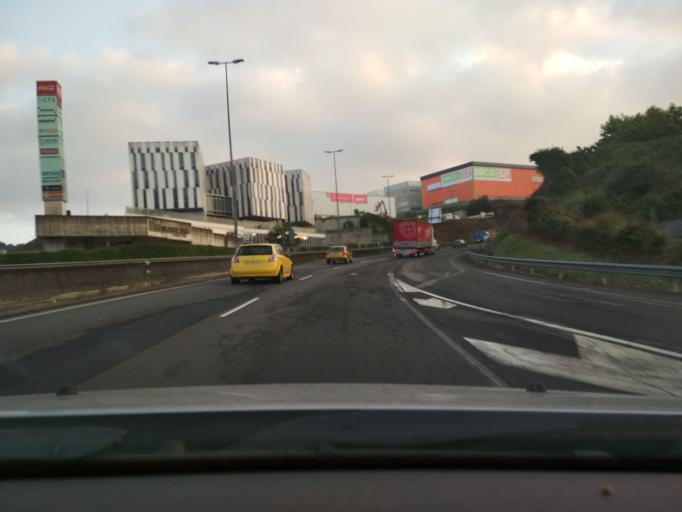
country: ES
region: Galicia
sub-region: Provincia da Coruna
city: Santiago de Compostela
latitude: 42.9033
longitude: -8.5119
